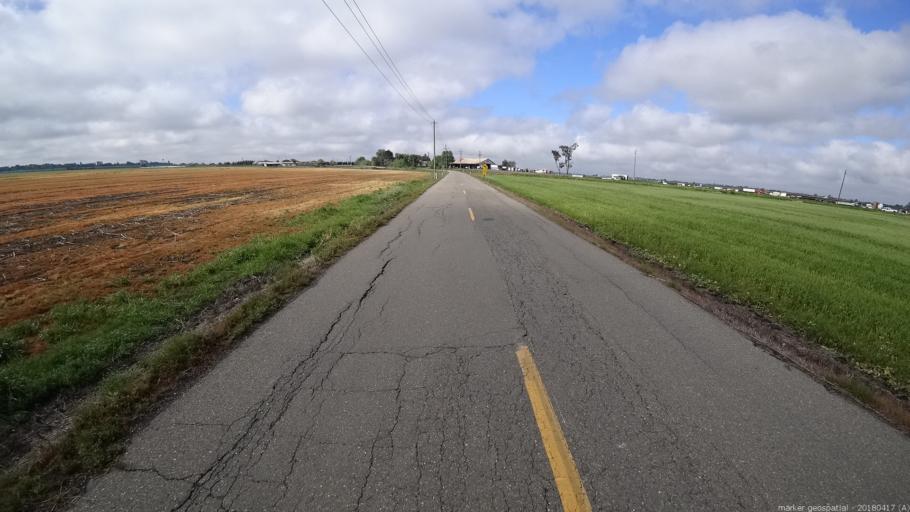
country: US
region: California
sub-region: Sacramento County
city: Walnut Grove
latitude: 38.2604
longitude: -121.5567
